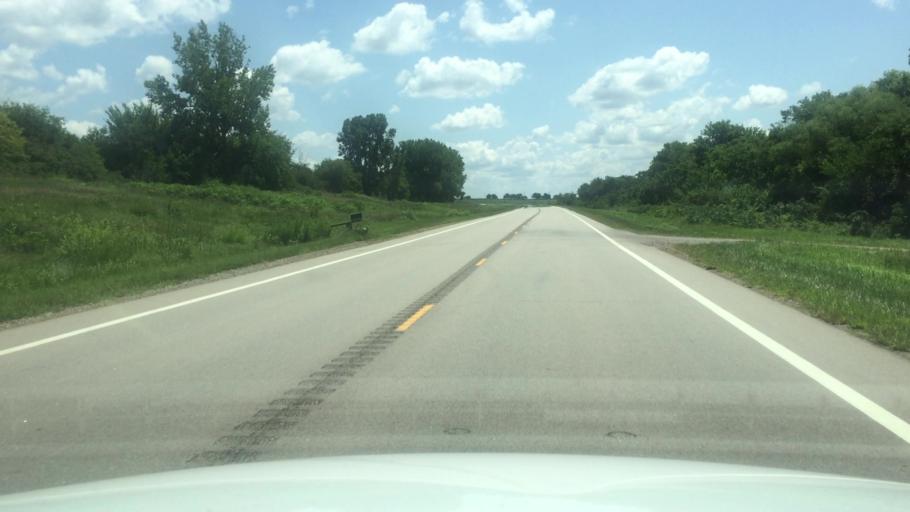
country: US
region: Kansas
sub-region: Brown County
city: Horton
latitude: 39.6204
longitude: -95.3493
